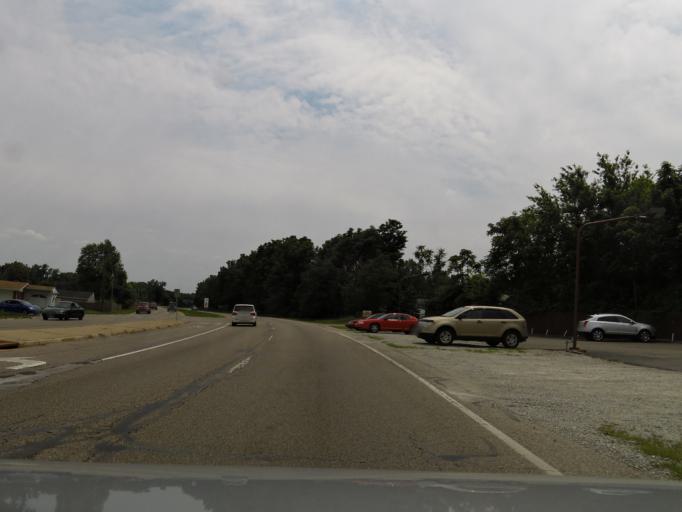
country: US
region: Ohio
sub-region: Montgomery County
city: Riverside
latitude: 39.7656
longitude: -84.1236
